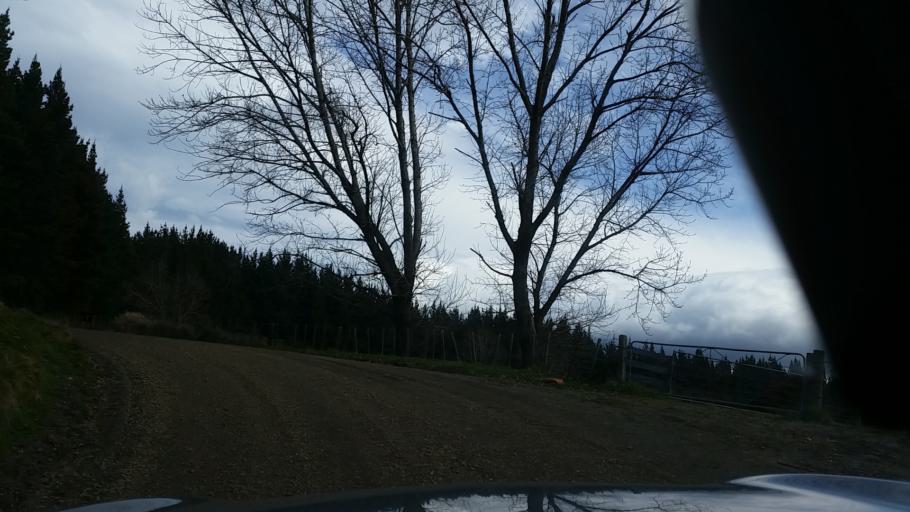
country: NZ
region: Hawke's Bay
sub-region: Napier City
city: Napier
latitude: -39.2281
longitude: 176.9866
